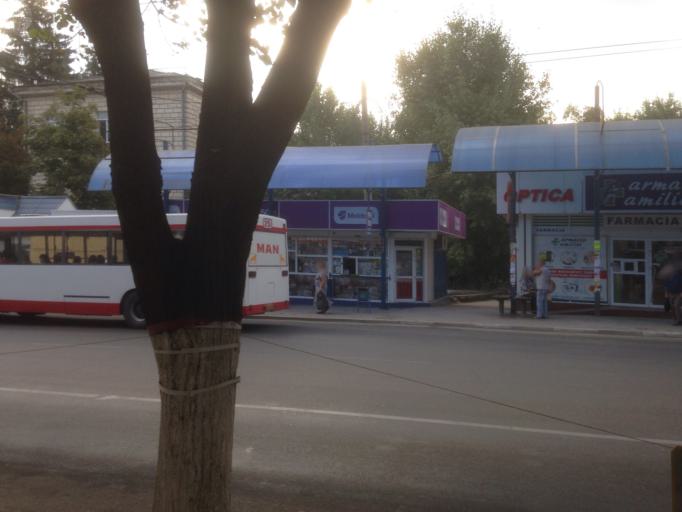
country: MD
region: Balti
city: Balti
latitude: 47.7641
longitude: 27.9307
